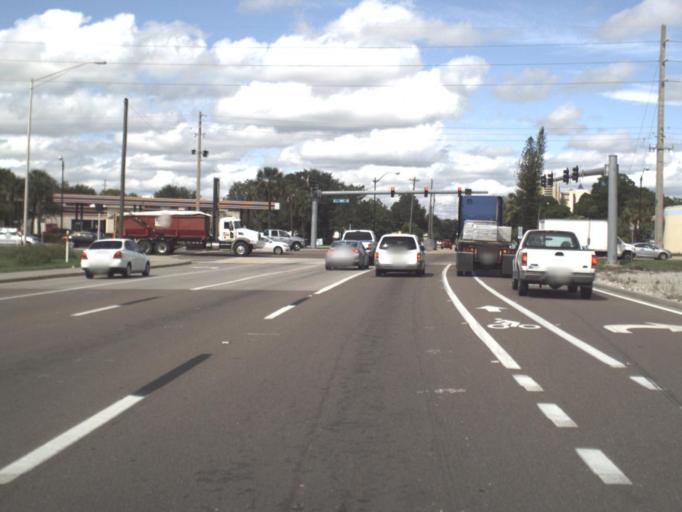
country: US
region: Florida
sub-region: Lee County
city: Fort Myers
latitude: 26.6403
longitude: -81.8605
